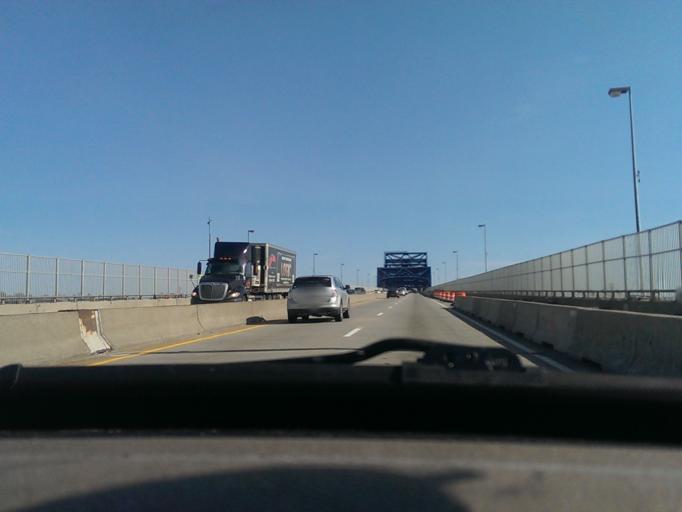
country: US
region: Massachusetts
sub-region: Bristol County
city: Fall River
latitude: 41.7097
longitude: -71.1713
